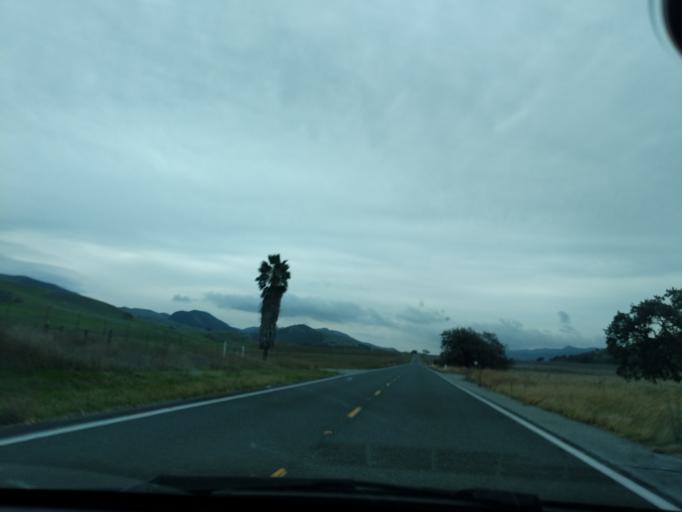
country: US
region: California
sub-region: San Benito County
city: Ridgemark
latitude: 36.6838
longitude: -121.2611
